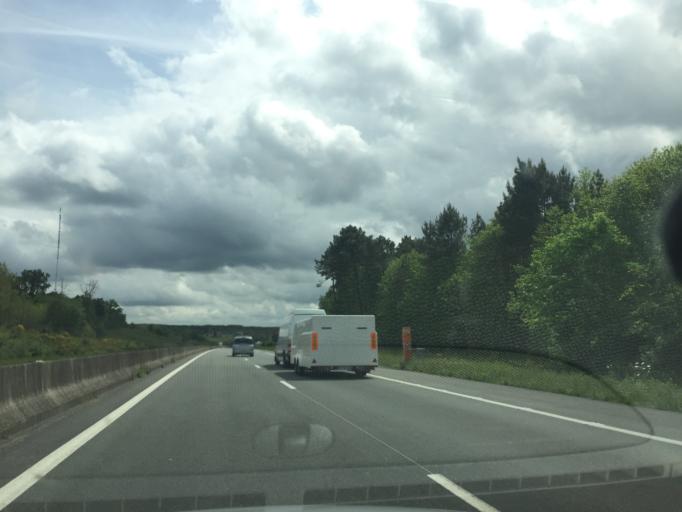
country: FR
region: Pays de la Loire
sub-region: Departement de la Sarthe
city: Mayet
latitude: 47.7788
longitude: 0.3118
